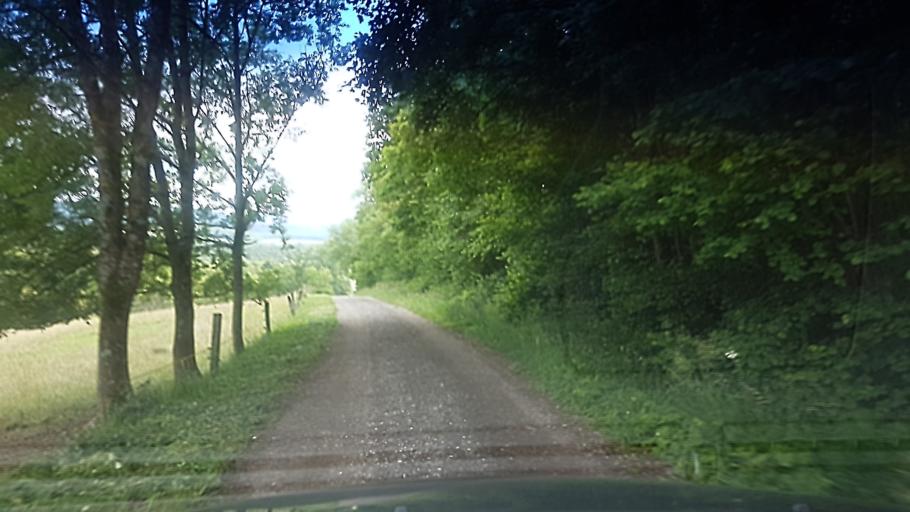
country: DE
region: Bavaria
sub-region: Upper Franconia
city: Buttenheim
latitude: 49.8326
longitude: 11.0532
